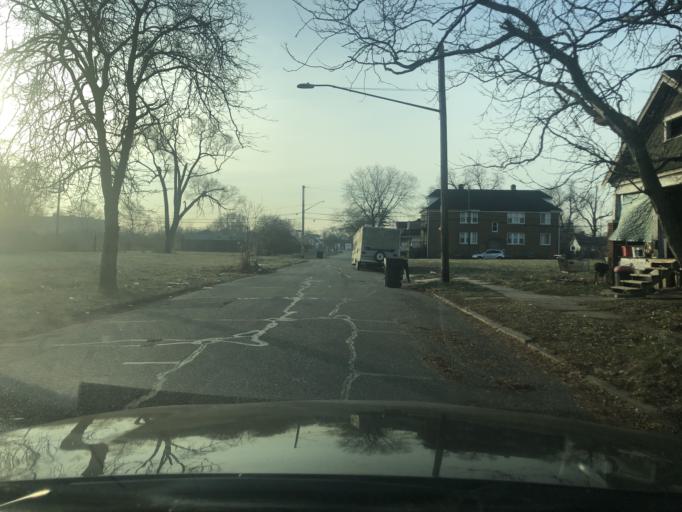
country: US
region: Michigan
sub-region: Wayne County
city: Highland Park
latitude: 42.4015
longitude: -83.1309
